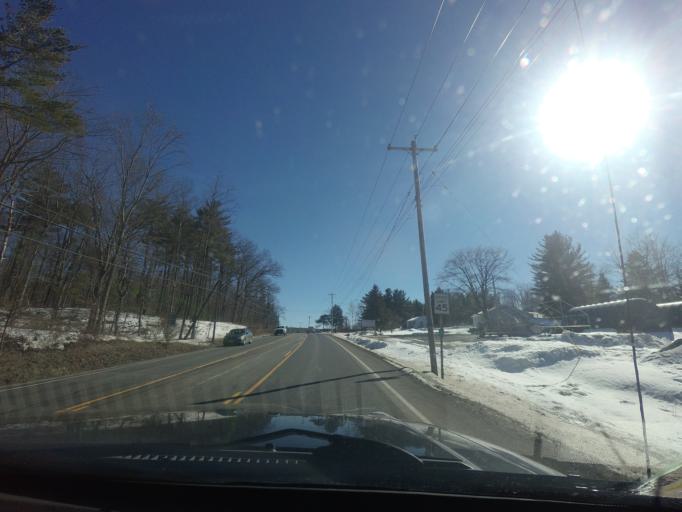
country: US
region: New York
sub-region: Rensselaer County
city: Nassau
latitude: 42.5337
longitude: -73.6592
